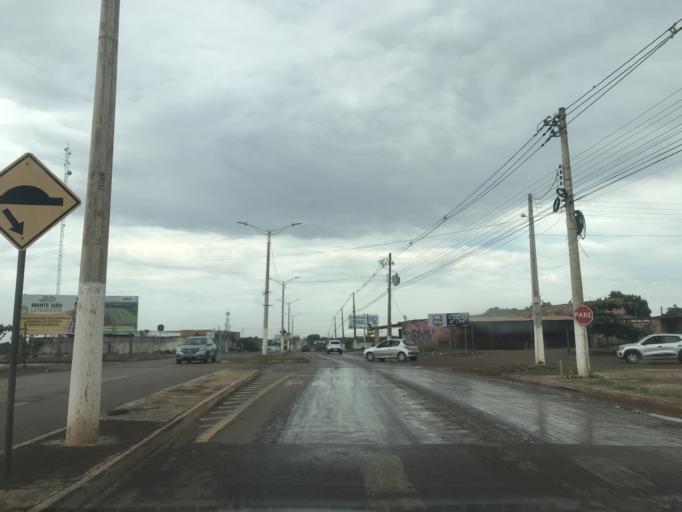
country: BR
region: Goias
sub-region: Luziania
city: Luziania
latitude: -16.2150
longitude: -47.9311
